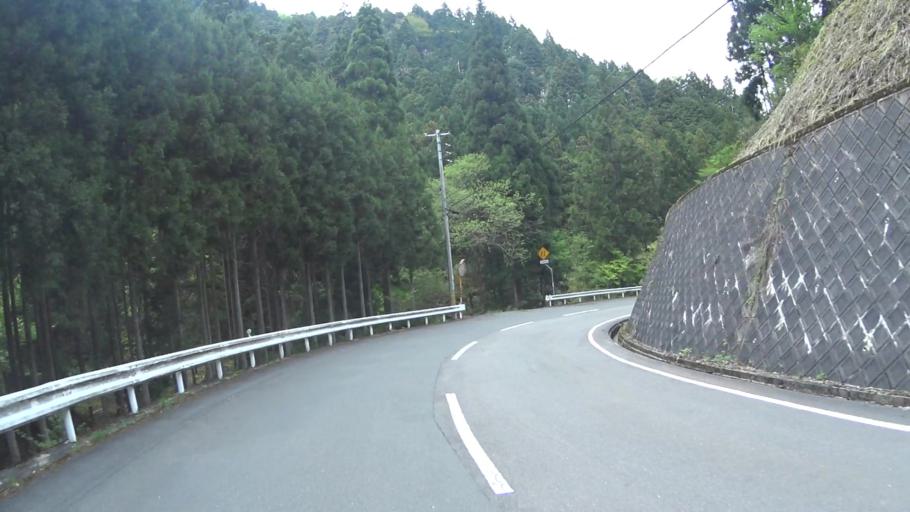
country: JP
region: Kyoto
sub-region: Kyoto-shi
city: Kamigyo-ku
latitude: 35.1829
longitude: 135.7334
